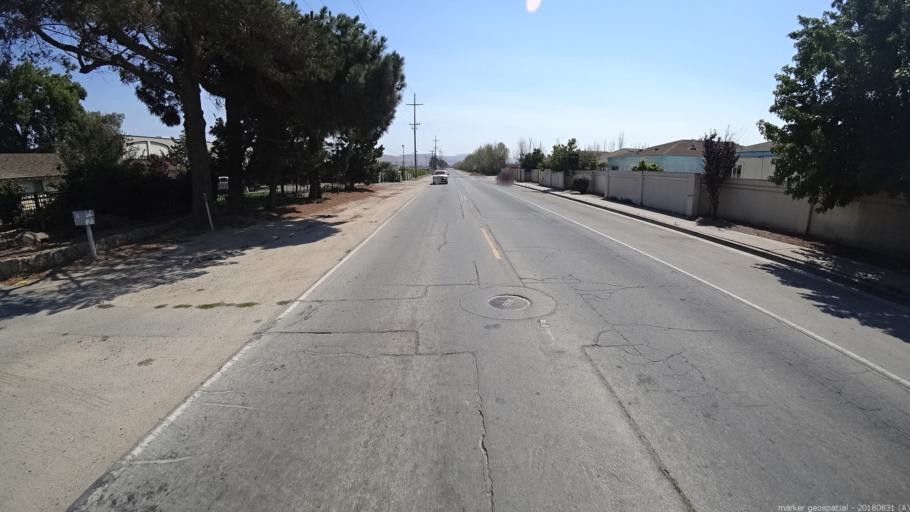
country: US
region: California
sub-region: Monterey County
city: Soledad
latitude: 36.4259
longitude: -121.3106
